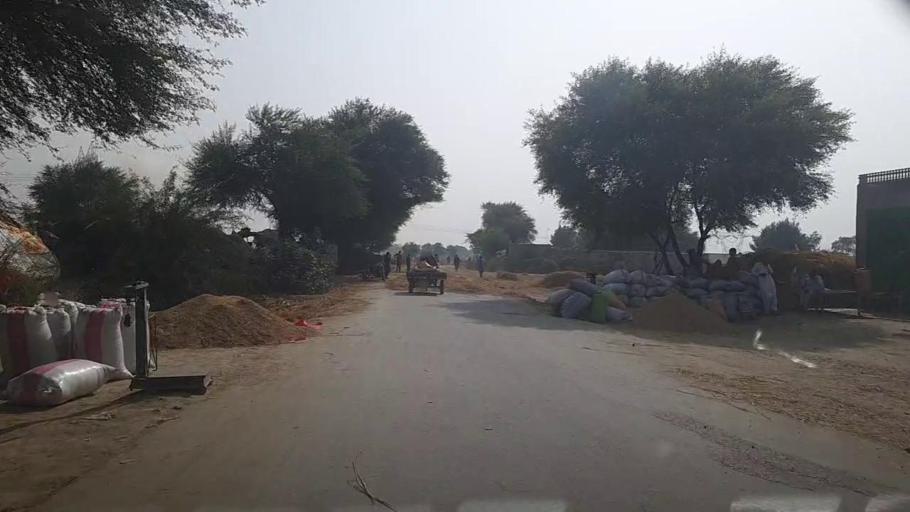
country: PK
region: Sindh
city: Kashmor
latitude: 28.4212
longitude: 69.5708
